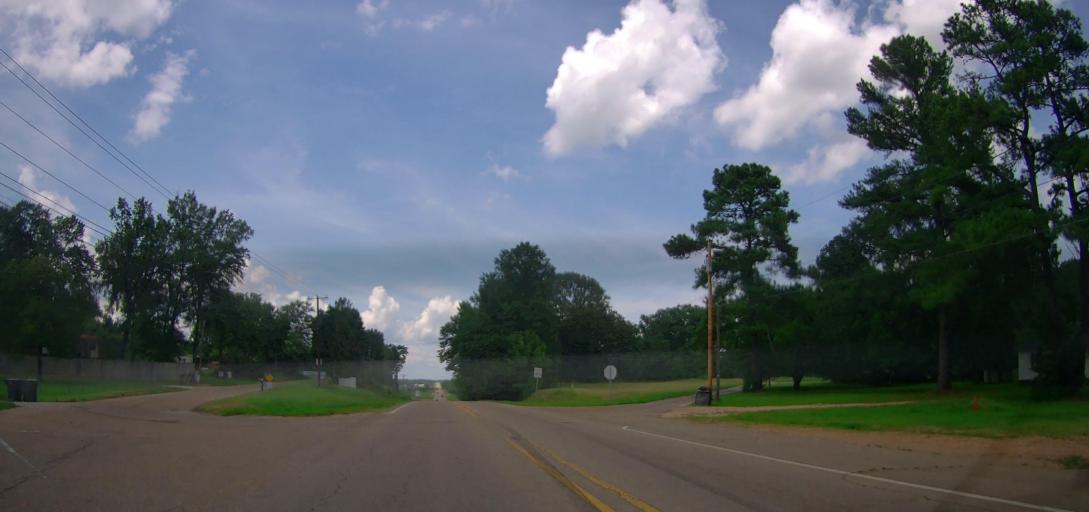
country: US
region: Mississippi
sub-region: Lee County
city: Shannon
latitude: 34.1307
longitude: -88.7193
